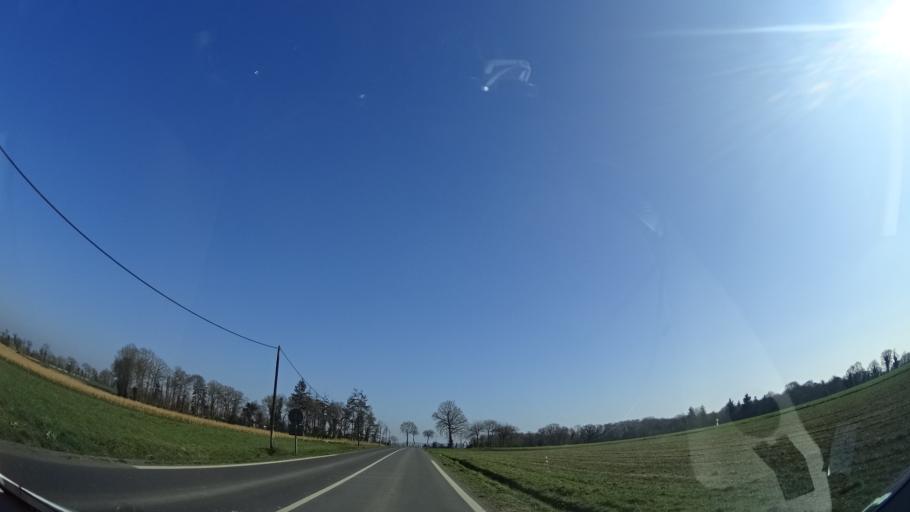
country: FR
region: Brittany
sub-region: Departement d'Ille-et-Vilaine
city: Meillac
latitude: 48.4144
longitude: -1.8370
